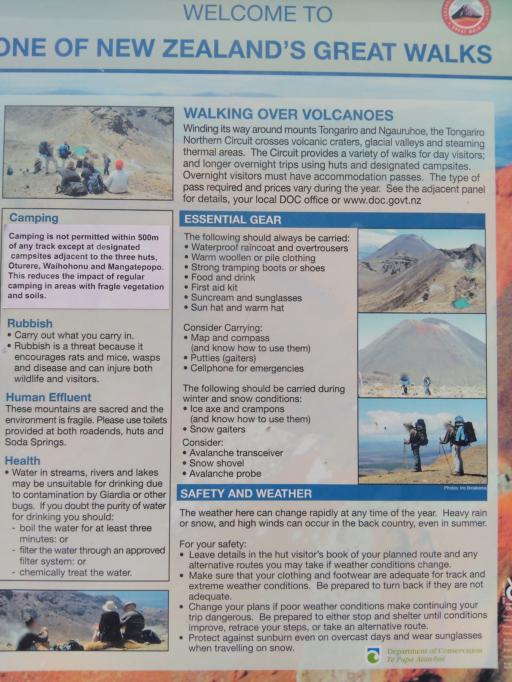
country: NZ
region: Manawatu-Wanganui
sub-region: Ruapehu District
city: Waiouru
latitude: -39.1995
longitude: 175.5430
